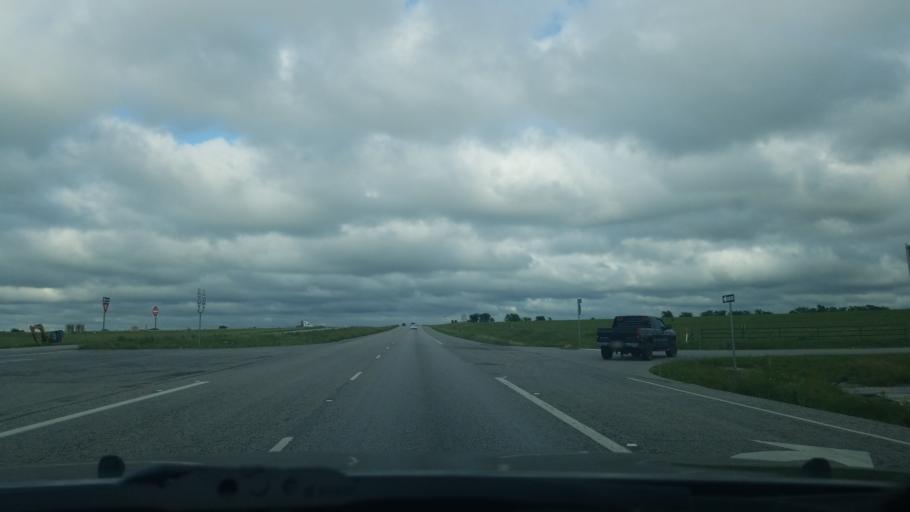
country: US
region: Texas
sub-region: Denton County
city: Ponder
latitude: 33.2398
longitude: -97.3419
